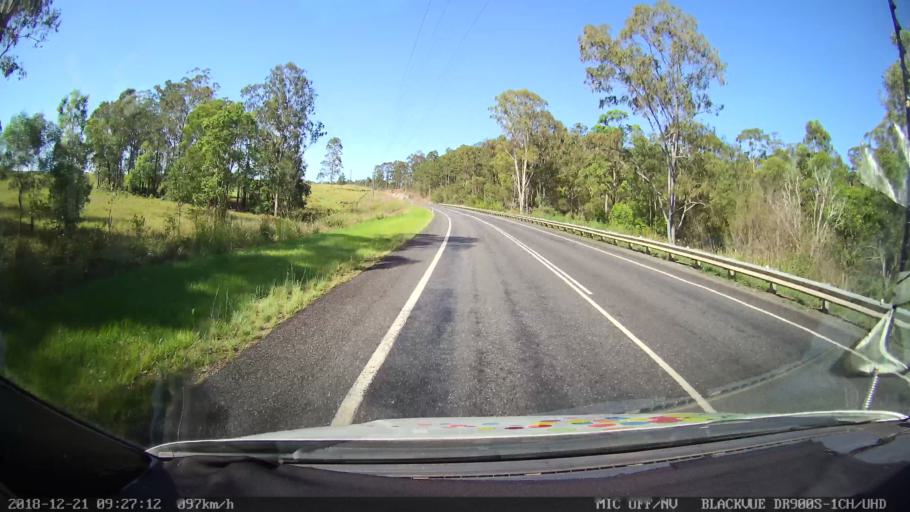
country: AU
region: New South Wales
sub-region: Clarence Valley
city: Maclean
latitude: -29.3998
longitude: 152.9922
